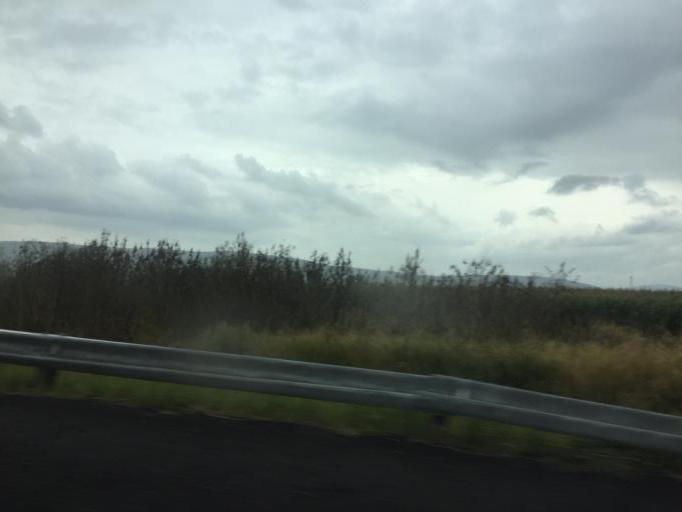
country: MX
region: Jalisco
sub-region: Zapotlan del Rey
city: Zapotlan del Rey
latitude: 20.4506
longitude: -102.8835
